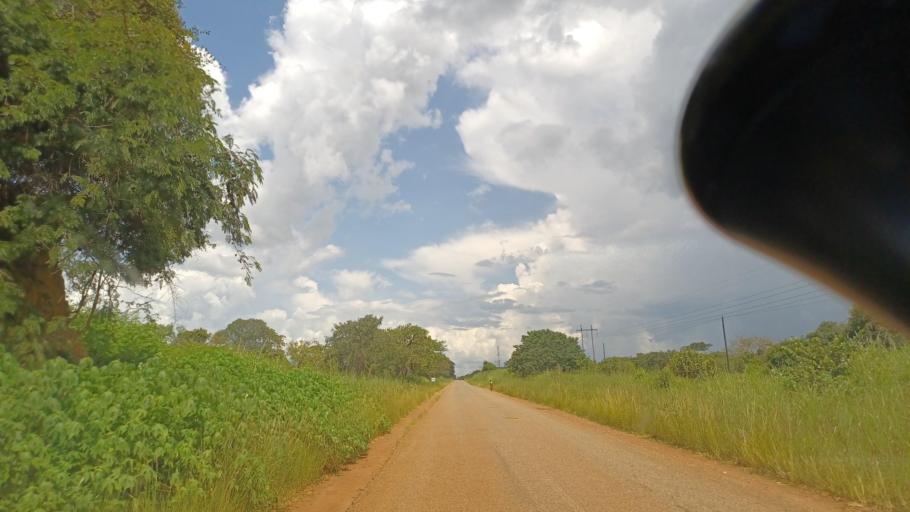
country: ZM
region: North-Western
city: Kasempa
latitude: -12.7860
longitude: 26.0114
